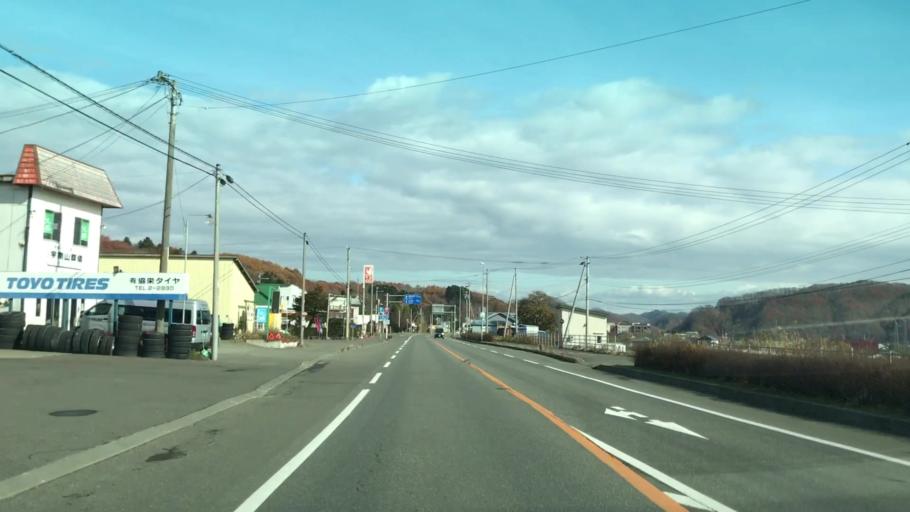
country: JP
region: Hokkaido
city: Shizunai-furukawacho
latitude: 42.5812
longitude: 142.1225
